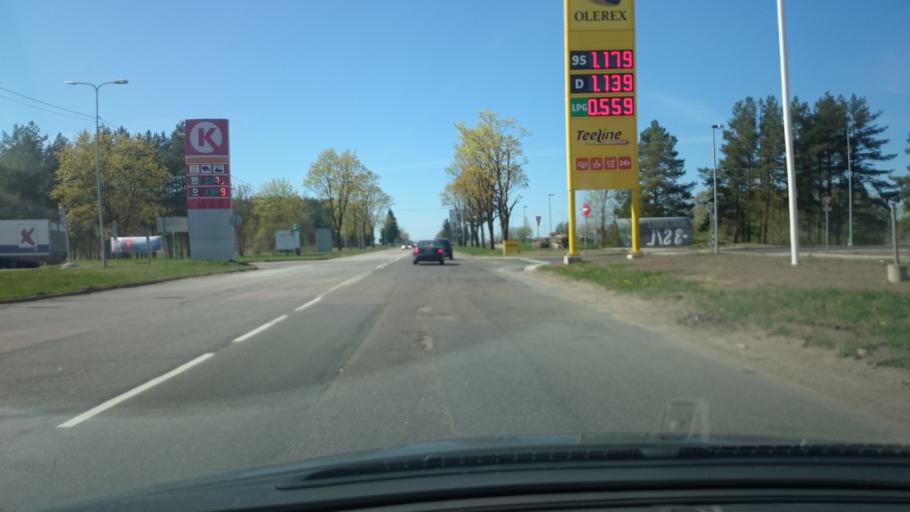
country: EE
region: Ida-Virumaa
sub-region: Narva linn
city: Narva
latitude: 59.3845
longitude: 28.1580
